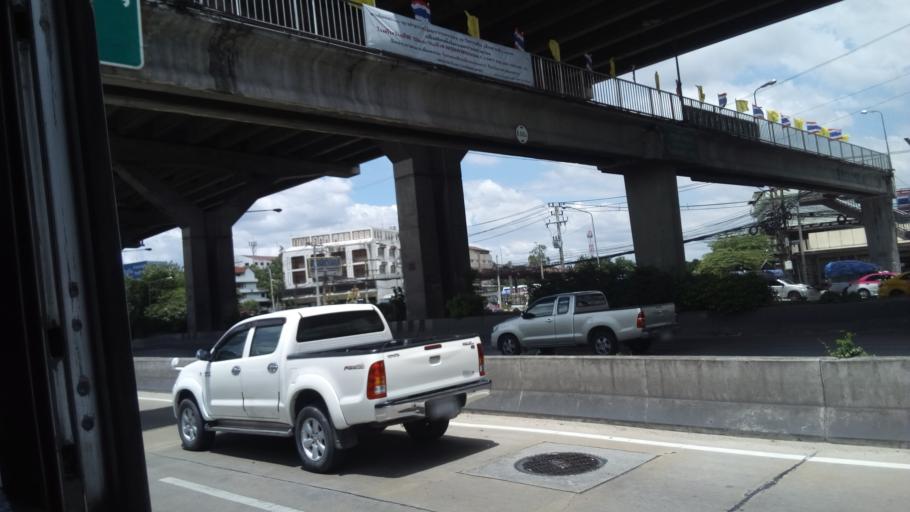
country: TH
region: Bangkok
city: Sai Mai
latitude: 13.9590
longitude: 100.6225
